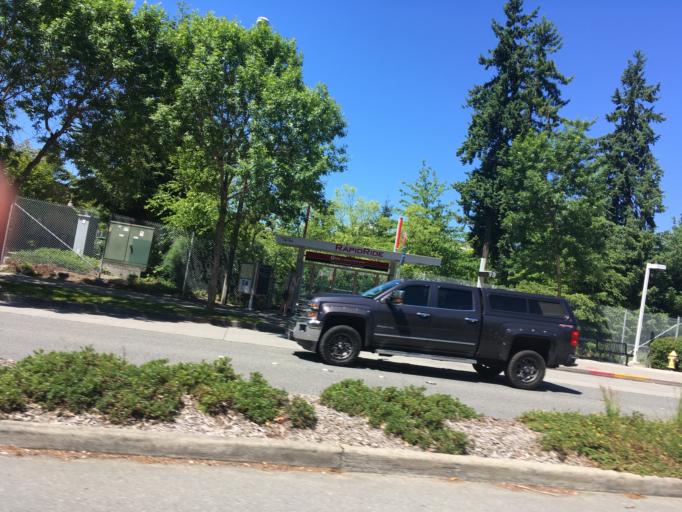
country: US
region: Washington
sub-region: King County
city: Redmond
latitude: 47.6445
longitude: -122.1322
